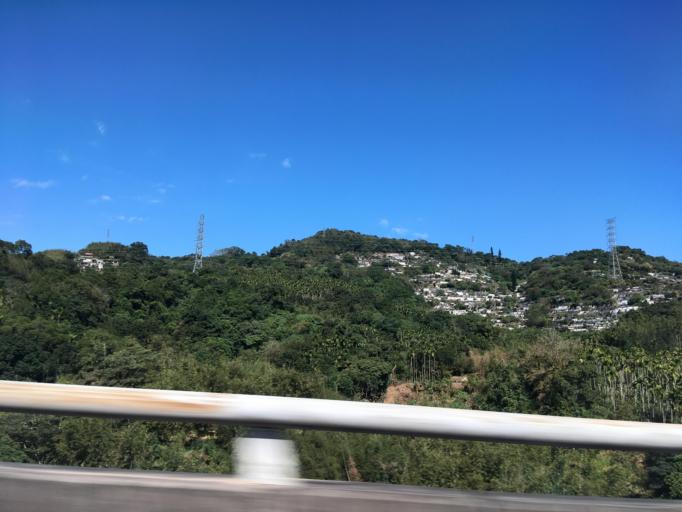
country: TW
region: Taipei
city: Taipei
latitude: 25.0068
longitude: 121.5781
